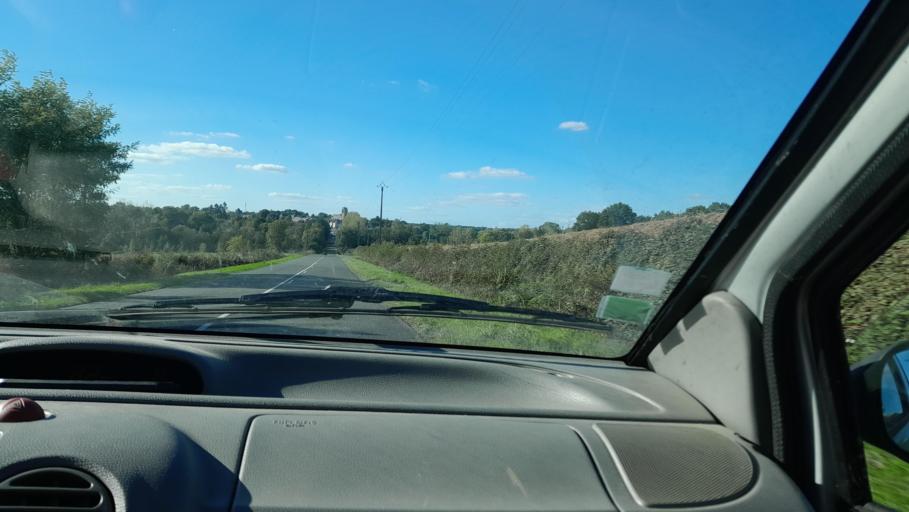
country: FR
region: Pays de la Loire
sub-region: Departement de la Mayenne
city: Cosse-le-Vivien
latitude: 47.9567
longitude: -0.9672
